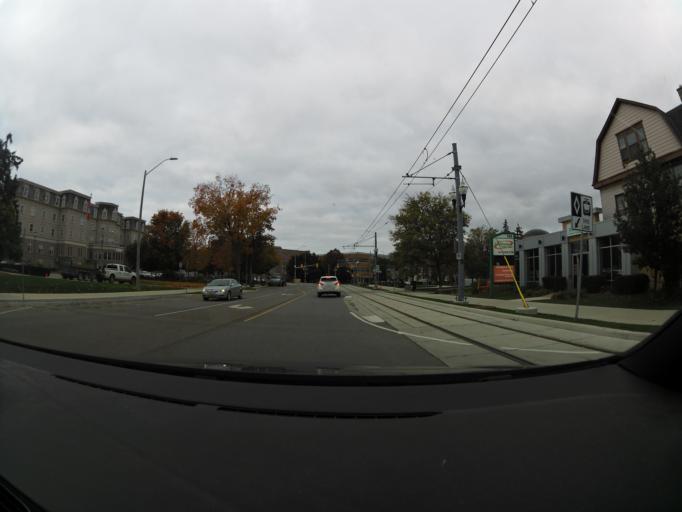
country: CA
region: Ontario
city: Waterloo
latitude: 43.4609
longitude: -80.5202
